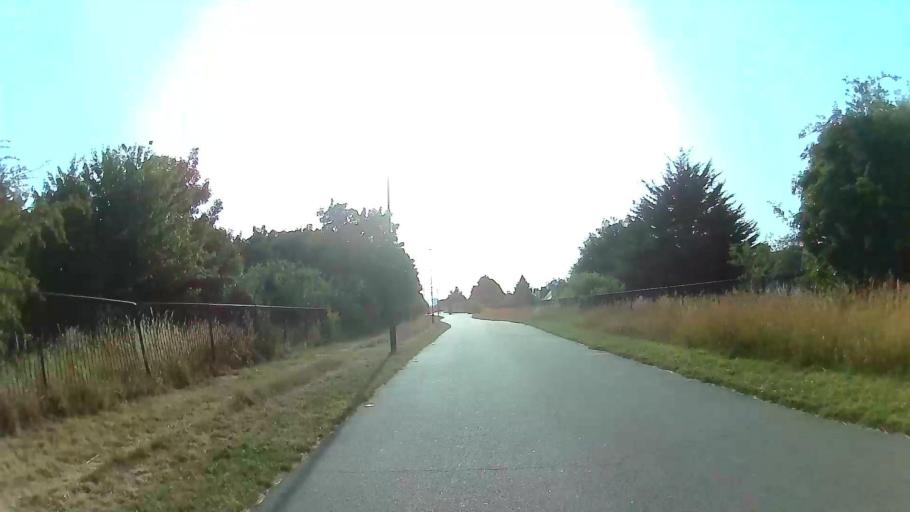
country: GB
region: England
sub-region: Greater London
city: East Ham
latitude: 51.5213
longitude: 0.0541
